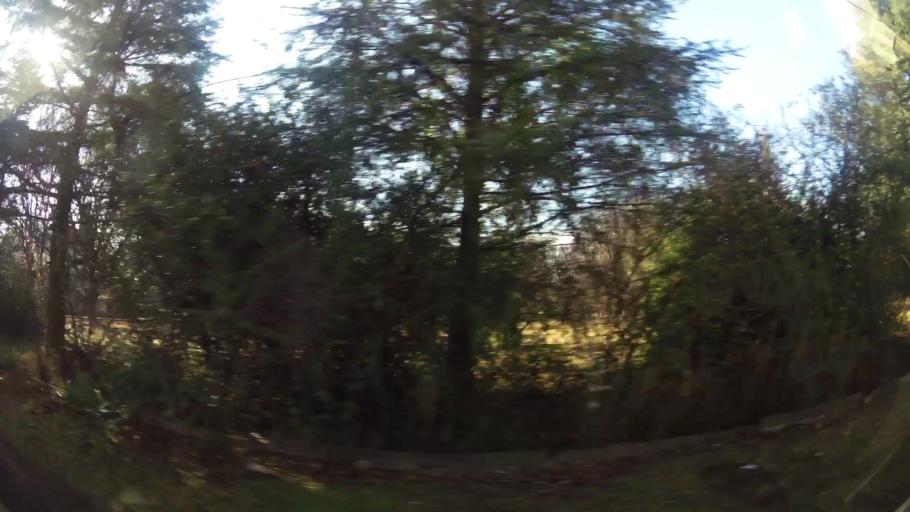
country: ZA
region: Gauteng
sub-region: Sedibeng District Municipality
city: Meyerton
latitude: -26.4990
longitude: 28.0690
